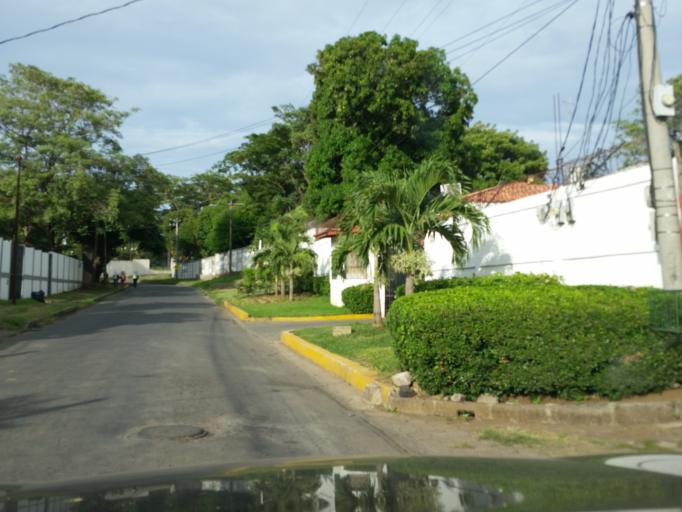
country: NI
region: Managua
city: Managua
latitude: 12.0958
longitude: -86.2303
